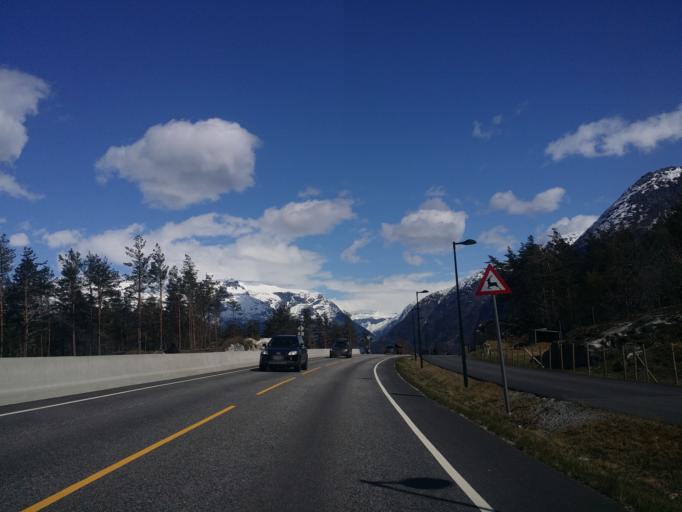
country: NO
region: Hordaland
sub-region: Ulvik
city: Ulvik
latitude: 60.4701
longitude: 6.8589
